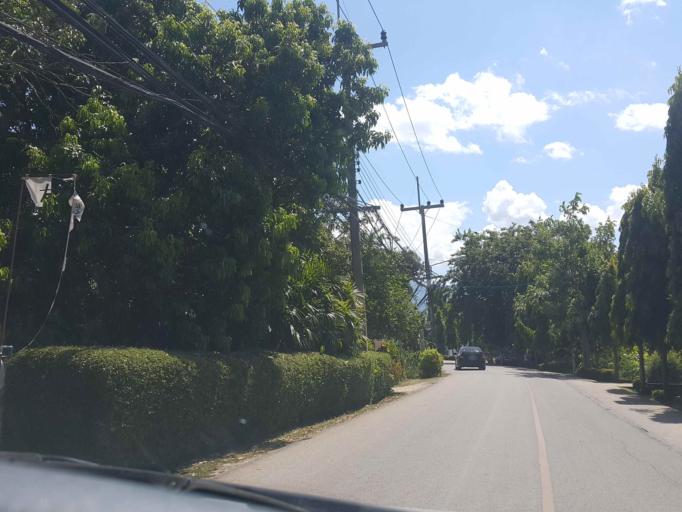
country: TH
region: Chiang Mai
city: San Sai
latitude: 18.8490
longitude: 99.0321
